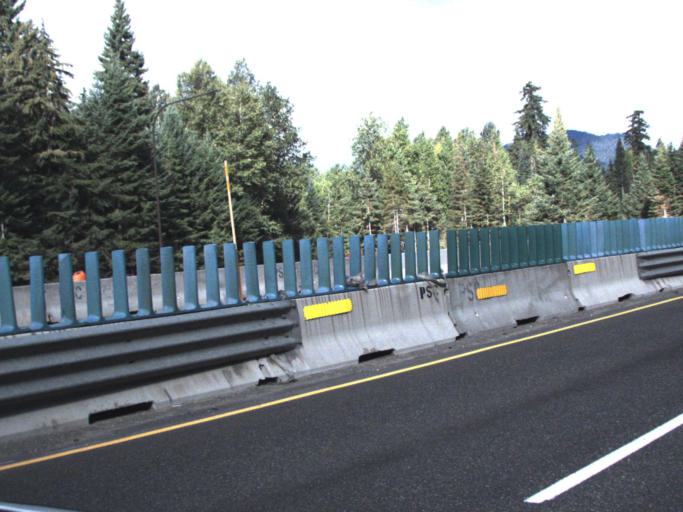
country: US
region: Washington
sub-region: Kittitas County
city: Cle Elum
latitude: 47.3193
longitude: -121.3210
